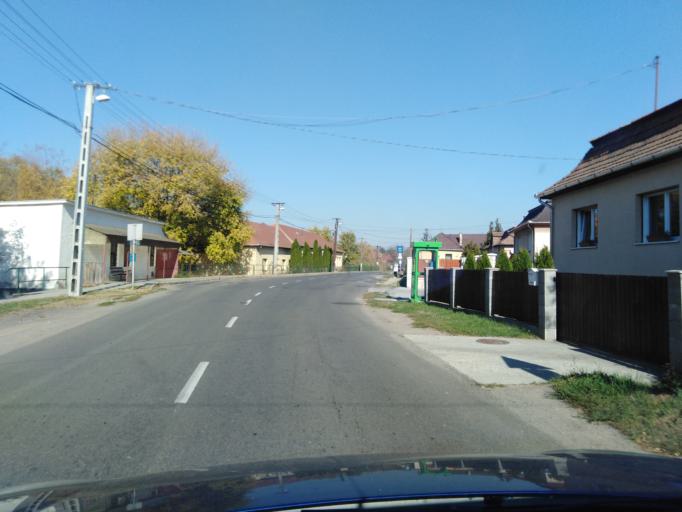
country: HU
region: Nograd
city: Karancslapujto
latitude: 48.1337
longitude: 19.7505
